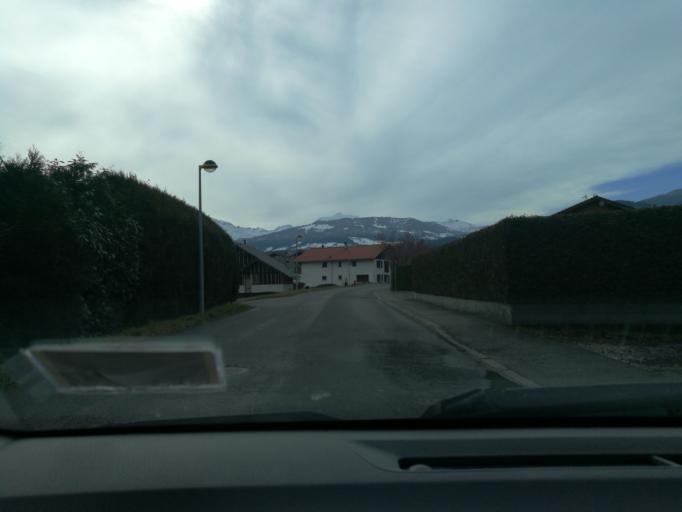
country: FR
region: Rhone-Alpes
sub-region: Departement de la Haute-Savoie
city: Sallanches
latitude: 45.9482
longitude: 6.6275
